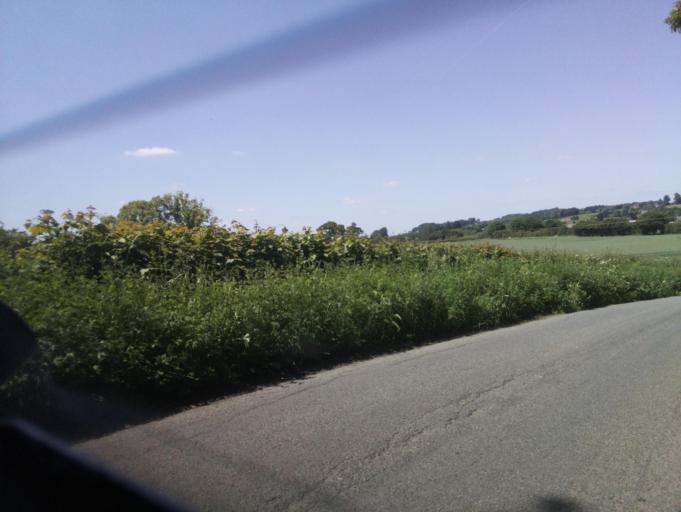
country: GB
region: England
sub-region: Wiltshire
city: Bremhill
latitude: 51.4419
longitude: -2.0236
